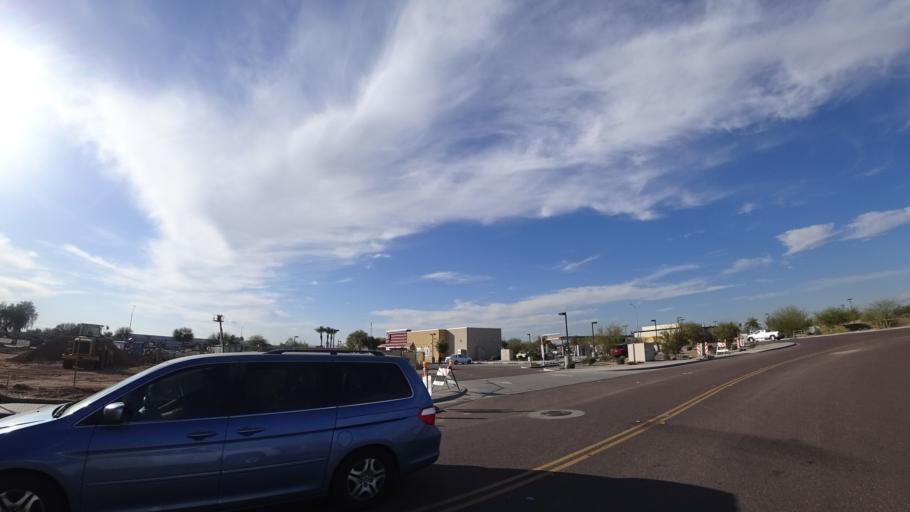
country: US
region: Arizona
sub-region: Maricopa County
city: Tolleson
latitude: 33.4594
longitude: -112.2021
